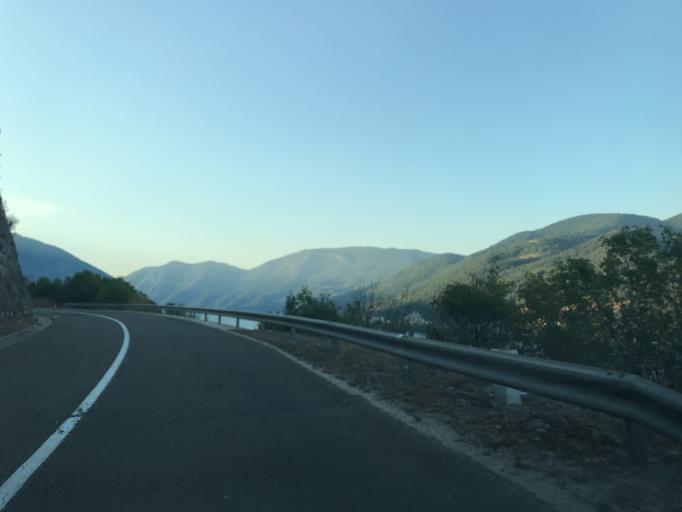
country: RO
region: Mehedinti
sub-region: Comuna Svinita
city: Svinita
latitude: 44.5548
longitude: 22.0266
